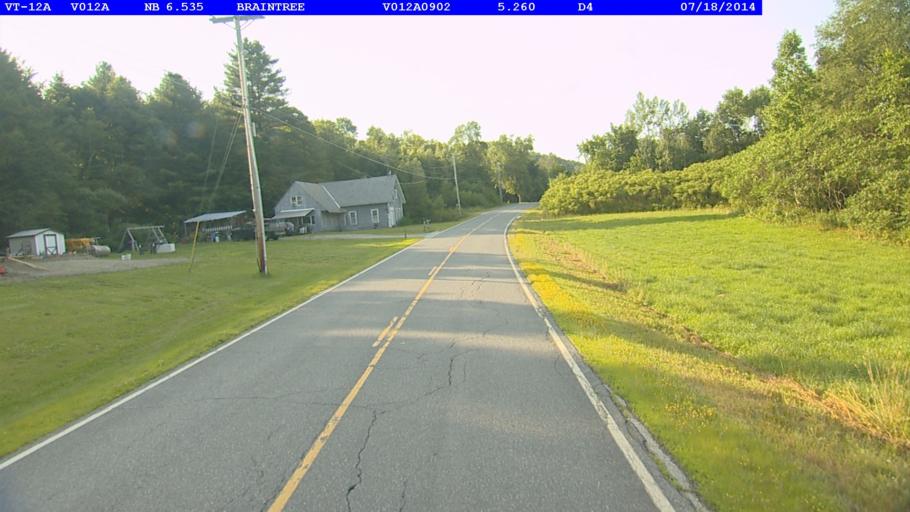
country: US
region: Vermont
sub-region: Orange County
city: Randolph
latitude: 43.9830
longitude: -72.7522
